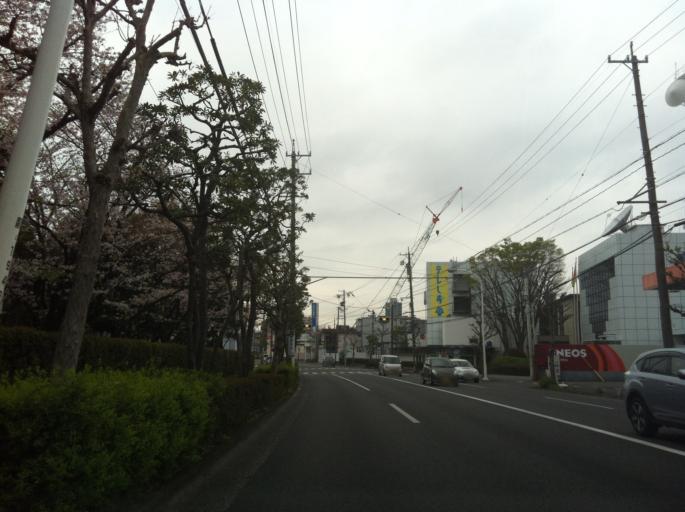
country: JP
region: Shizuoka
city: Shizuoka-shi
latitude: 34.9905
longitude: 138.4270
